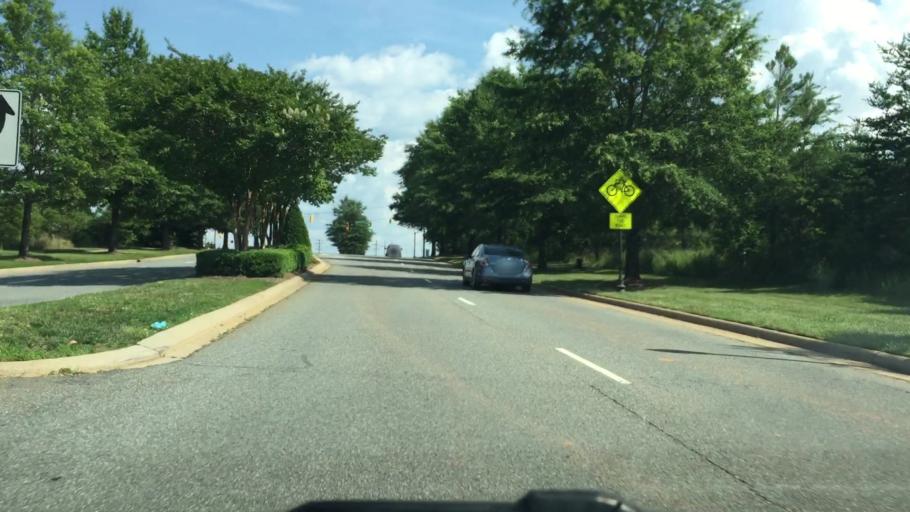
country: US
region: North Carolina
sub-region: Iredell County
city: Mooresville
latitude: 35.5835
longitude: -80.8822
